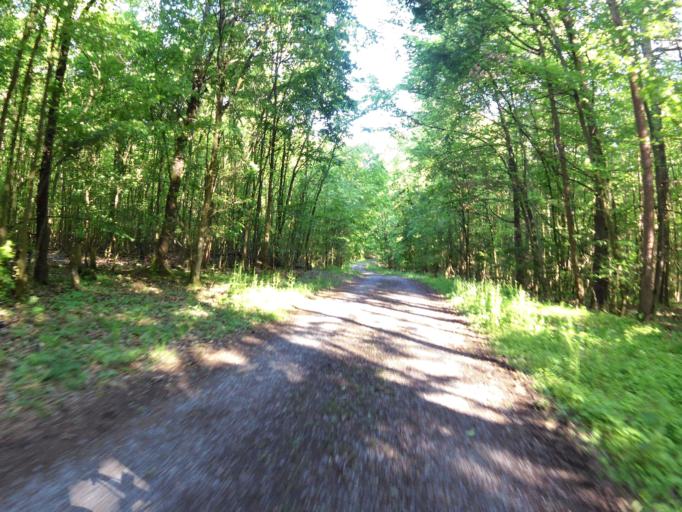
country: DE
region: Bavaria
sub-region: Regierungsbezirk Unterfranken
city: Reichenberg
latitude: 49.7489
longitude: 9.9172
